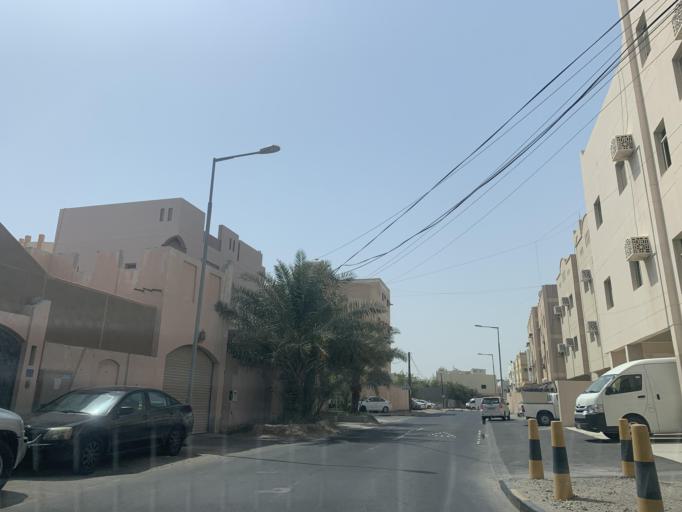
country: BH
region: Northern
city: Madinat `Isa
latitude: 26.1872
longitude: 50.5444
